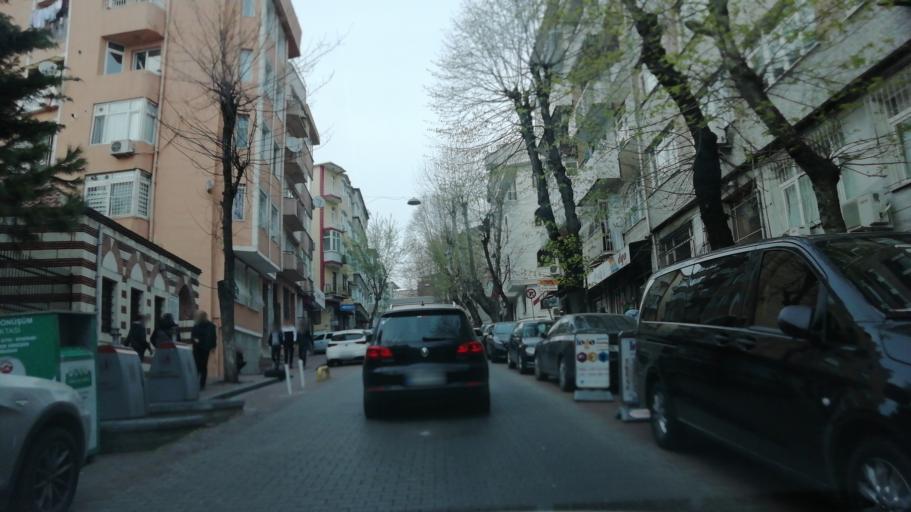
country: TR
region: Istanbul
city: Istanbul
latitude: 41.0151
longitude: 28.9491
